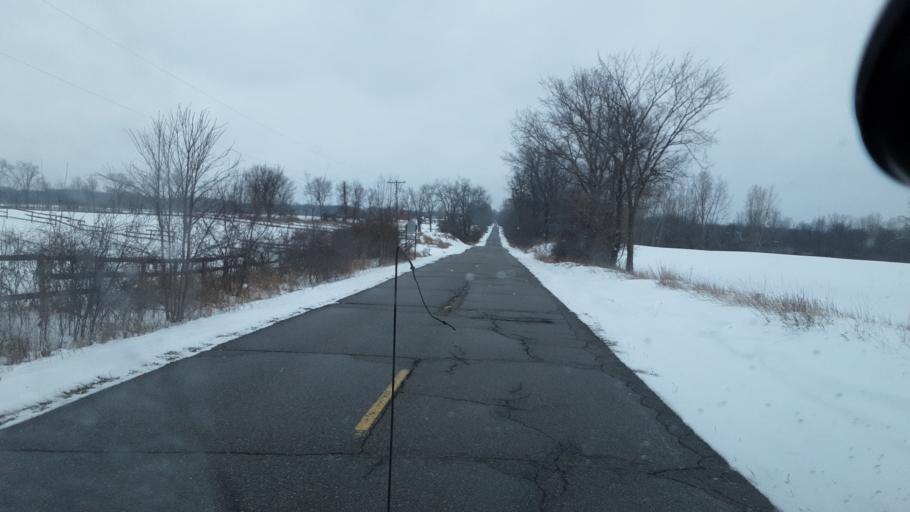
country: US
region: Michigan
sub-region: Ingham County
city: Leslie
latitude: 42.4647
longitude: -84.3941
